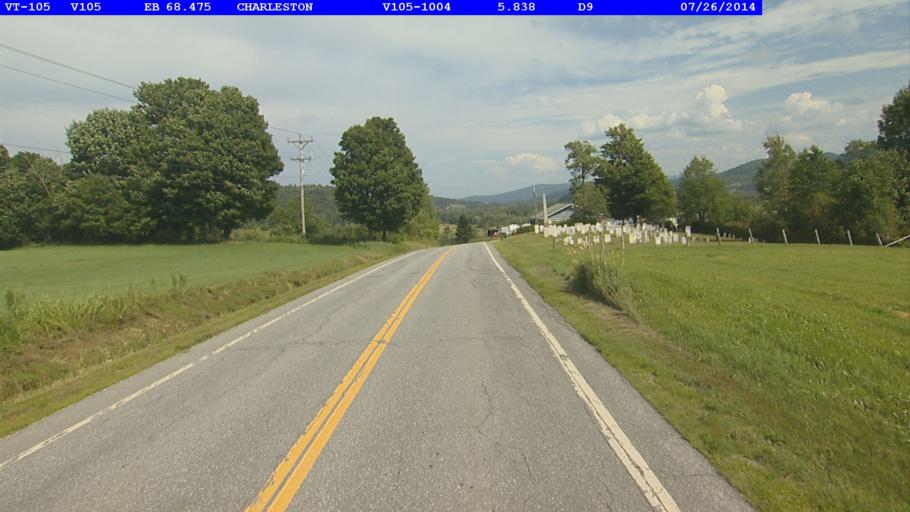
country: US
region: Vermont
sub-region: Orleans County
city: Newport
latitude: 44.8440
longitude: -72.0131
